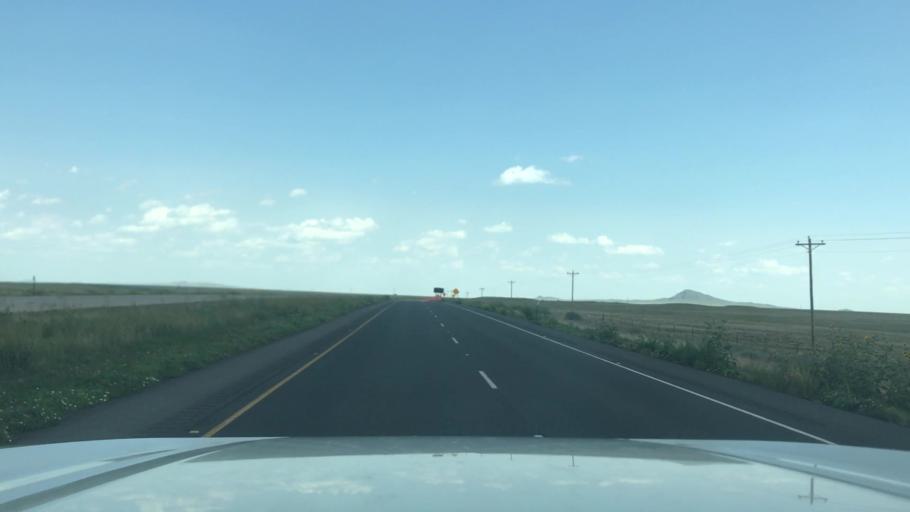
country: US
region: New Mexico
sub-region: Union County
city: Clayton
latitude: 36.6181
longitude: -103.6913
